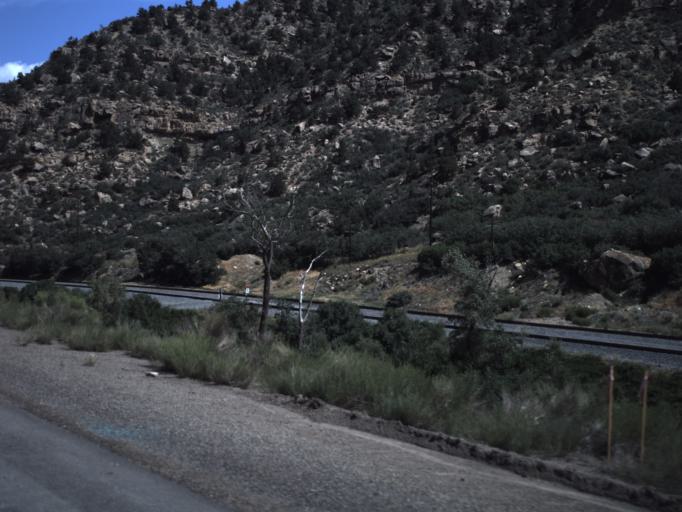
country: US
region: Utah
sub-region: Carbon County
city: Helper
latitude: 39.7881
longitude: -110.9289
